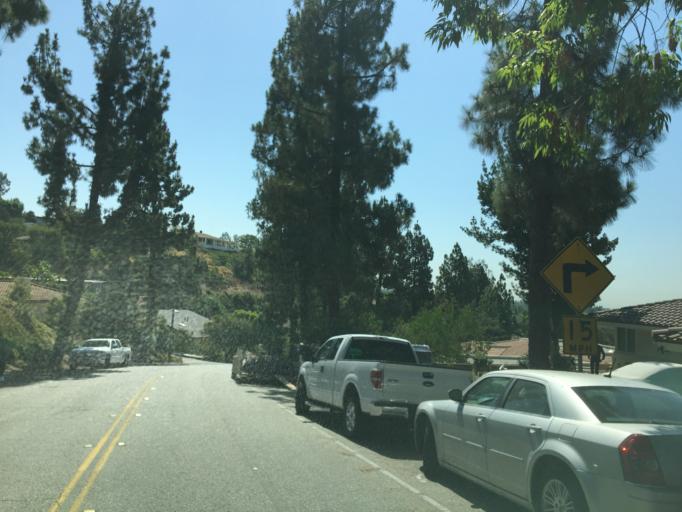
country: US
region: California
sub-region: Los Angeles County
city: Claremont
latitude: 34.1296
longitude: -117.7301
